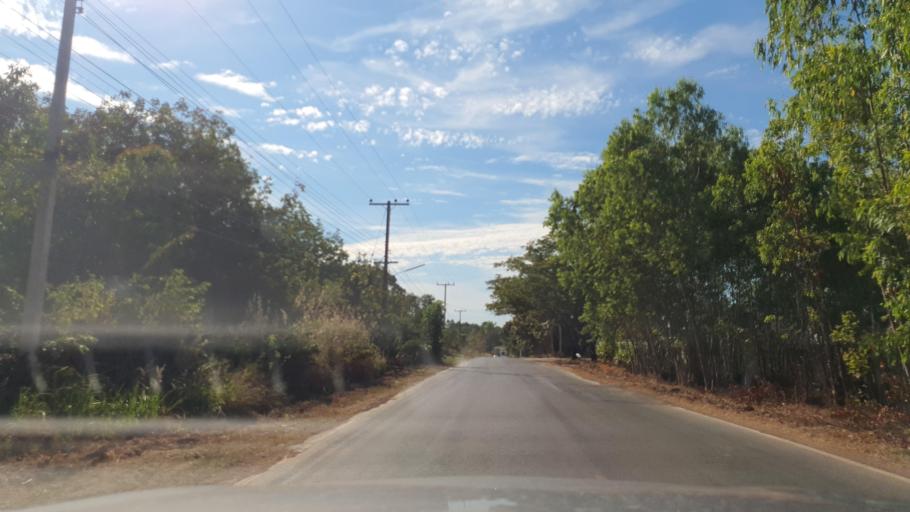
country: TH
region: Kalasin
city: Kuchinarai
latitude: 16.5419
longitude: 104.0870
